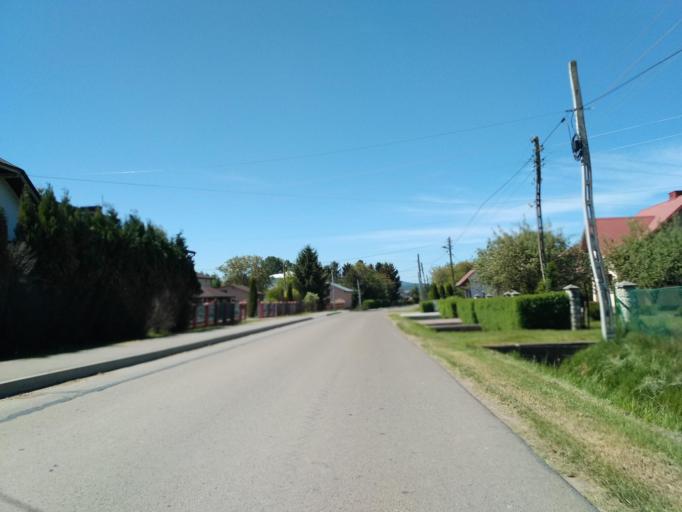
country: PL
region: Subcarpathian Voivodeship
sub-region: Powiat brzozowski
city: Jasionow
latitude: 49.6337
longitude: 21.9912
